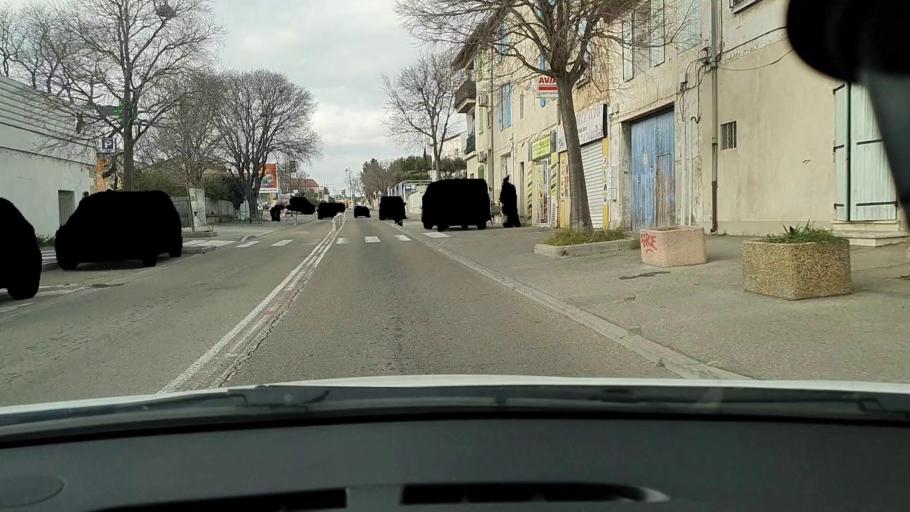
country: FR
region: Languedoc-Roussillon
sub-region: Departement du Gard
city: Beaucaire
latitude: 43.8106
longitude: 4.6367
